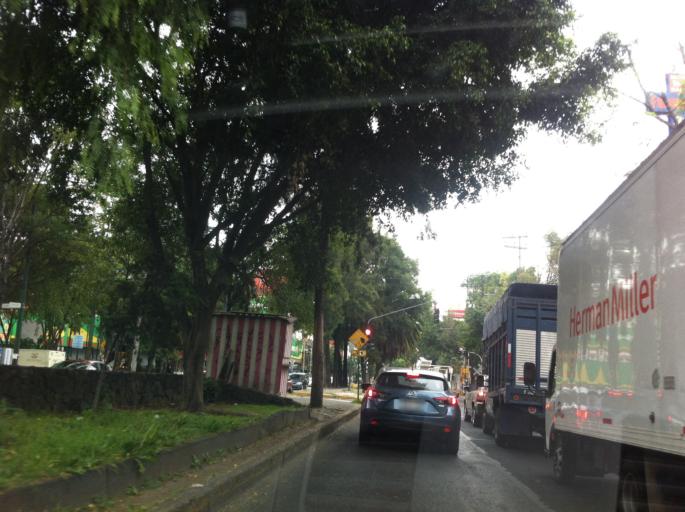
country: MX
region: Mexico City
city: Miguel Hidalgo
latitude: 19.4452
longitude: -99.1828
